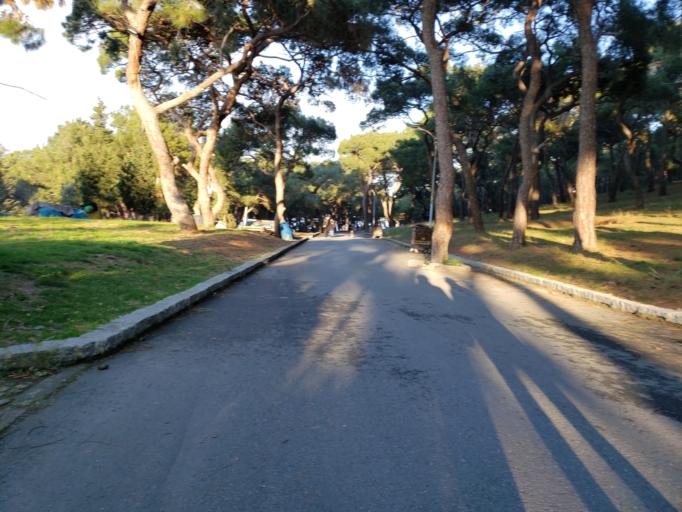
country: TR
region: Istanbul
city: Adalan
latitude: 40.8835
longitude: 29.0920
